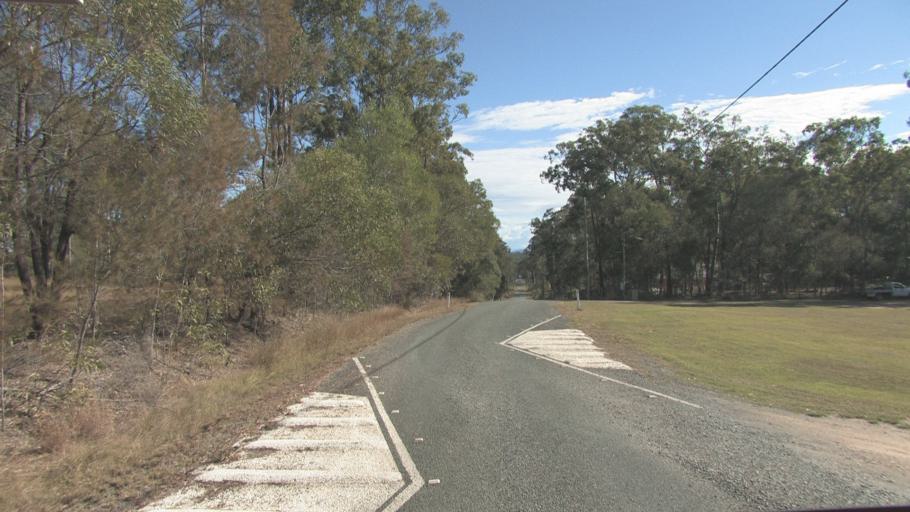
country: AU
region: Queensland
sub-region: Logan
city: Chambers Flat
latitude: -27.7974
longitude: 153.0802
